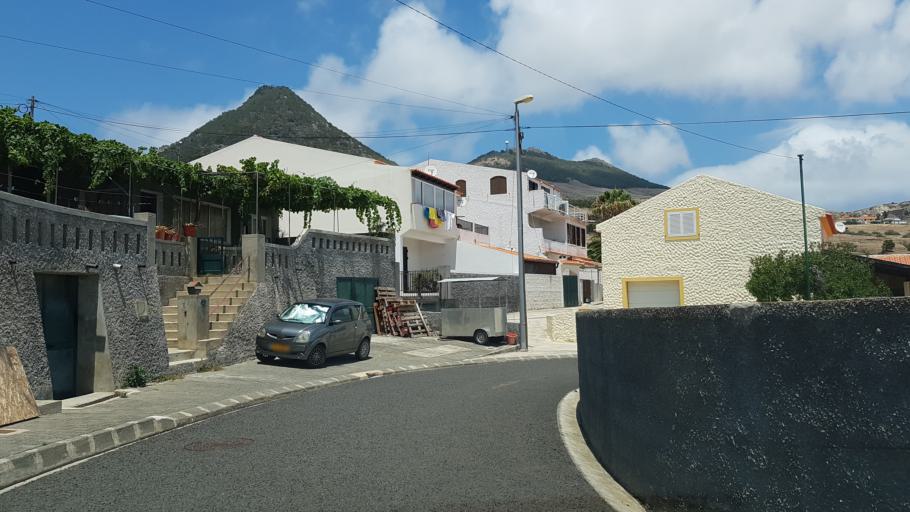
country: PT
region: Madeira
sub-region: Porto Santo
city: Vila de Porto Santo
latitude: 33.0694
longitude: -16.3388
